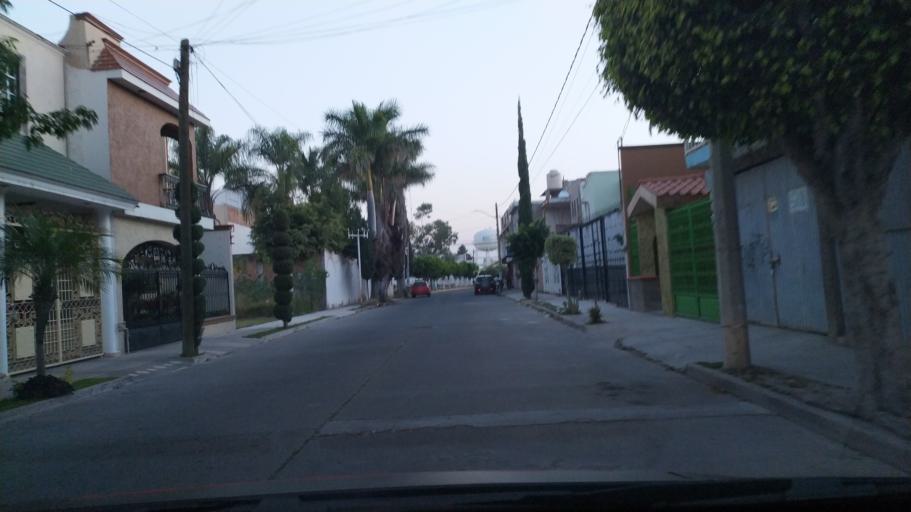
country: MX
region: Guanajuato
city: San Francisco del Rincon
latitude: 21.0107
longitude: -101.8607
